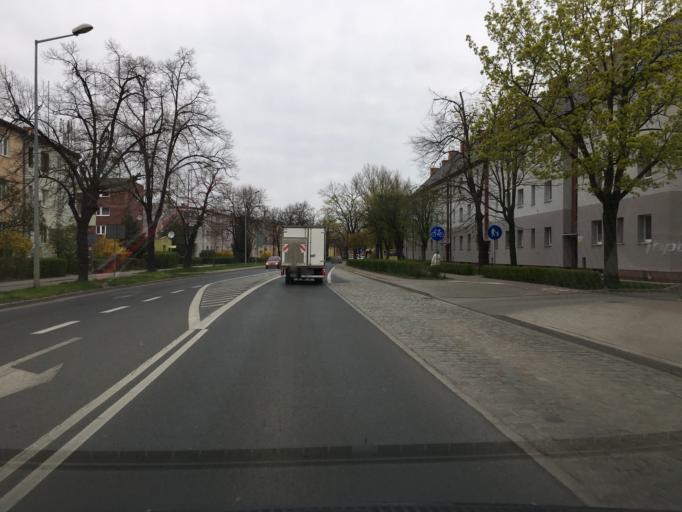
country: PL
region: Lower Silesian Voivodeship
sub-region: Legnica
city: Legnica
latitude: 51.1958
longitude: 16.1776
